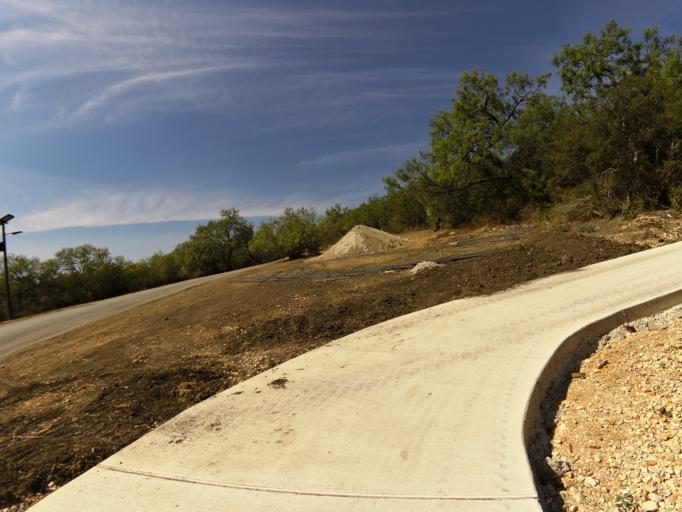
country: US
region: Texas
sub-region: Bexar County
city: San Antonio
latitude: 29.3842
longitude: -98.4324
